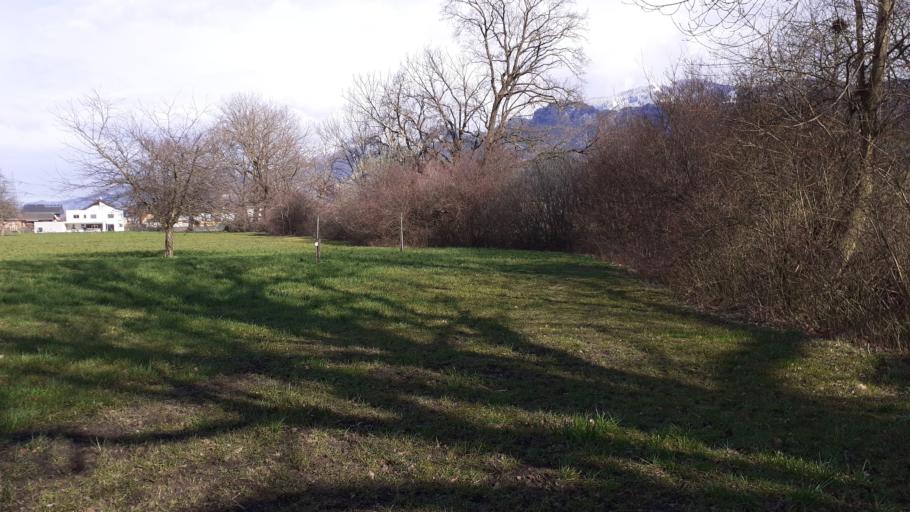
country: AT
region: Vorarlberg
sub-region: Politischer Bezirk Feldkirch
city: Mader
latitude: 47.3411
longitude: 9.6220
